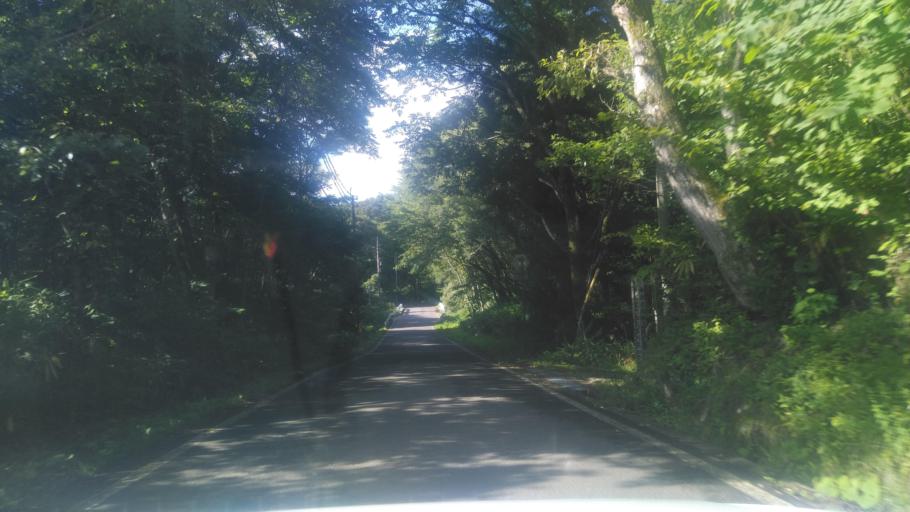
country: JP
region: Nagano
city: Nagano-shi
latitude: 36.7885
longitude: 138.1781
